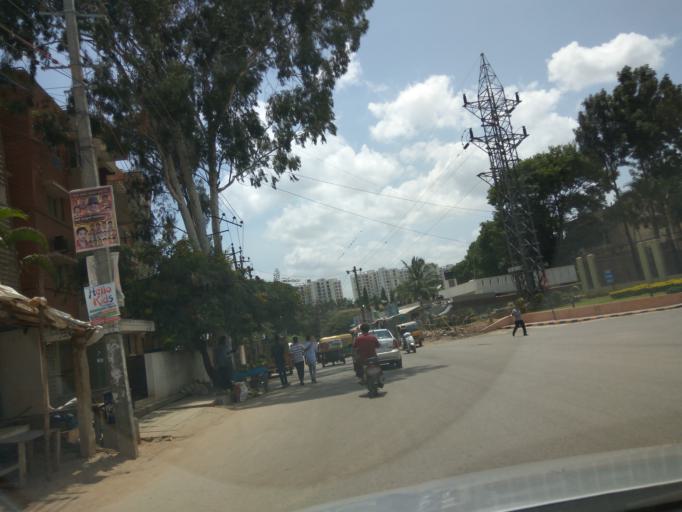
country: IN
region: Karnataka
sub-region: Bangalore Urban
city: Bangalore
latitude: 12.9859
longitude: 77.6714
